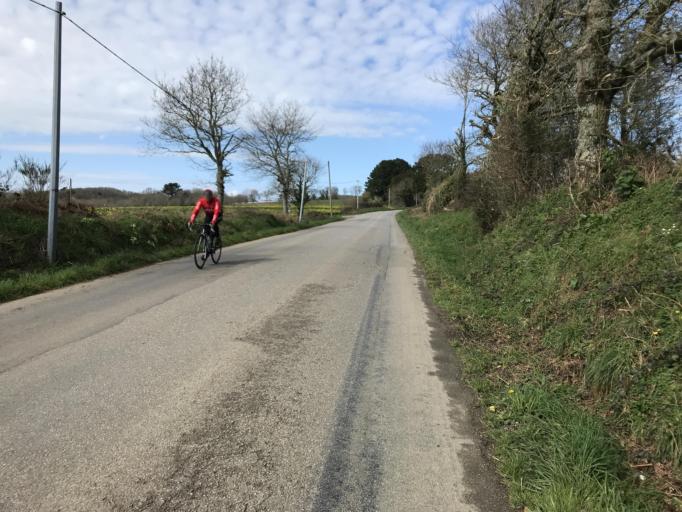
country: FR
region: Brittany
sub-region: Departement du Finistere
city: Daoulas
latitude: 48.3630
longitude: -4.2764
